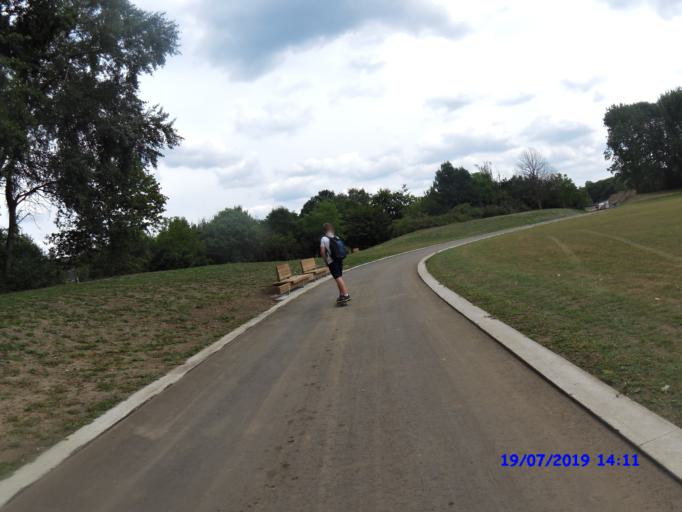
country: BE
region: Flanders
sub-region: Provincie Limburg
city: Hasselt
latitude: 50.9357
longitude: 5.3505
